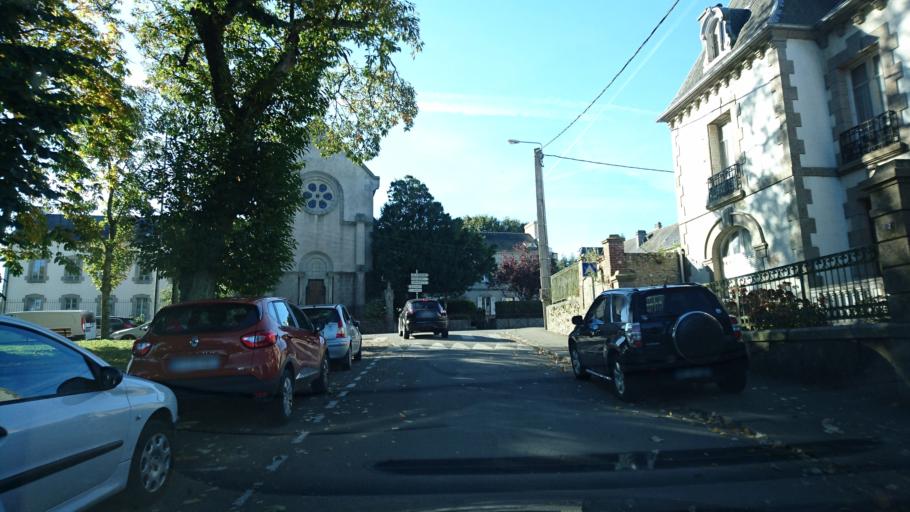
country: FR
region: Brittany
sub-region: Departement du Finistere
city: Saint-Renan
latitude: 48.4314
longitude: -4.6216
